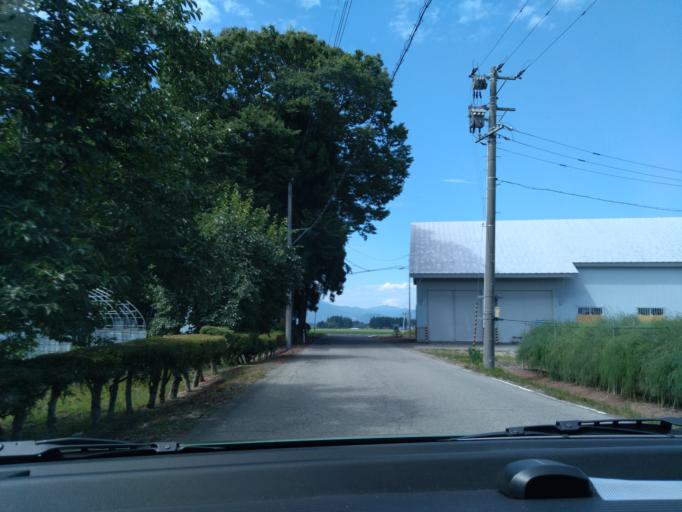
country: JP
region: Akita
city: Kakunodatemachi
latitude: 39.6123
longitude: 140.5945
